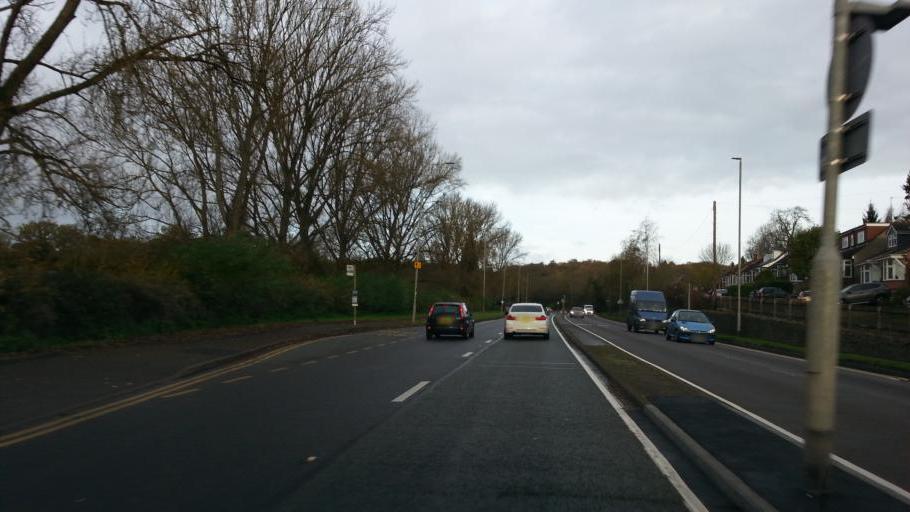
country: GB
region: England
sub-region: Leicestershire
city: Markfield
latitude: 52.6691
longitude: -1.2429
